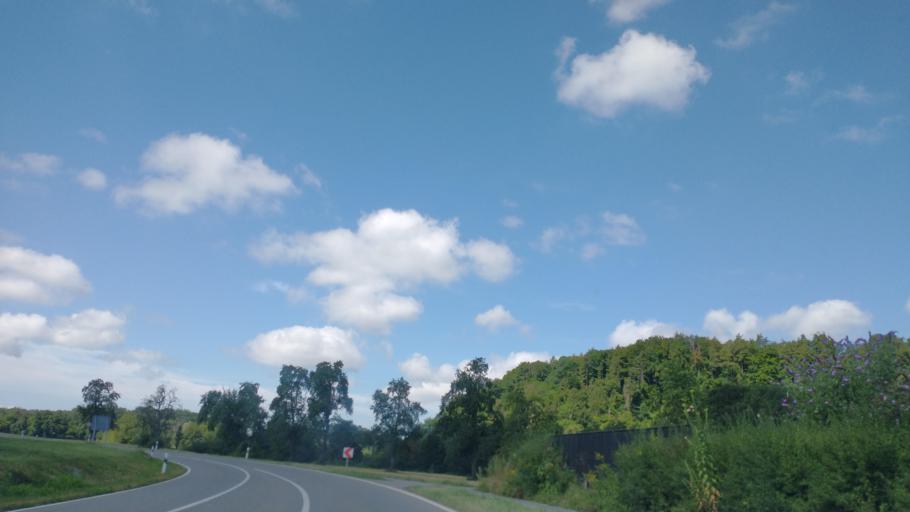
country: DE
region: Baden-Wuerttemberg
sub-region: Tuebingen Region
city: Kressbronn am Bodensee
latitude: 47.6346
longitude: 9.6262
